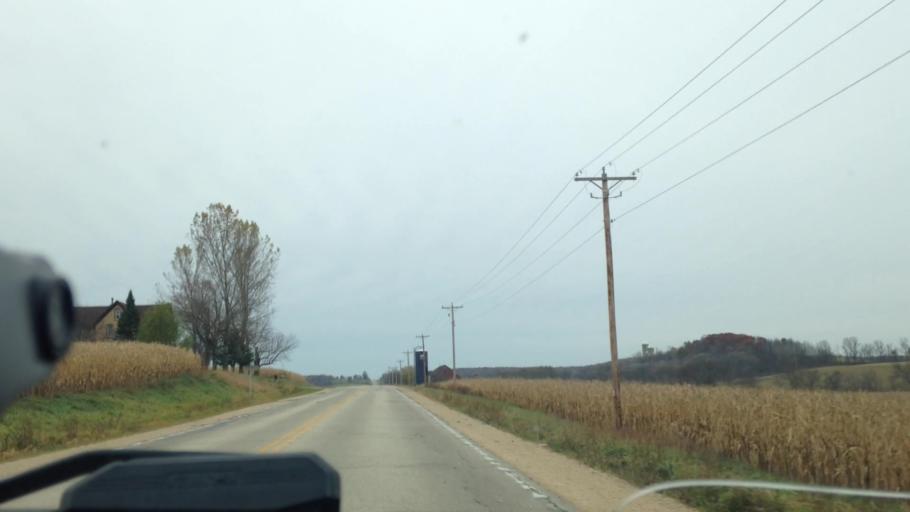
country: US
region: Wisconsin
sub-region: Dodge County
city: Mayville
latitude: 43.4774
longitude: -88.4998
